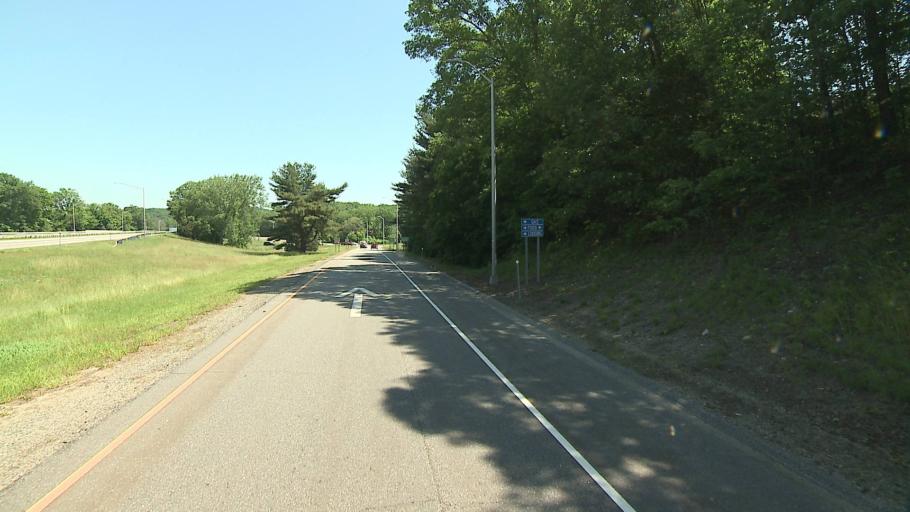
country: US
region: Connecticut
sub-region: New London County
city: Norwich
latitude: 41.5516
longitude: -72.1062
